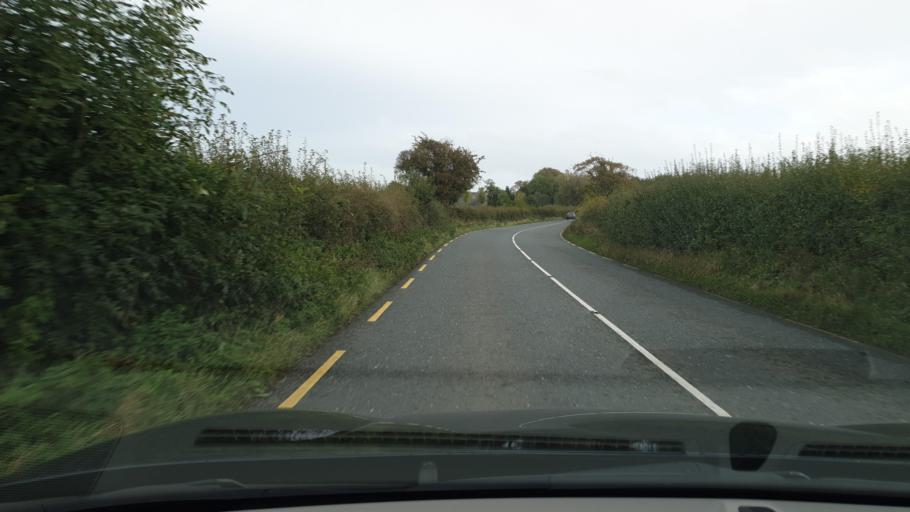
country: IE
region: Leinster
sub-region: An Mhi
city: Ratoath
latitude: 53.5024
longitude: -6.4376
